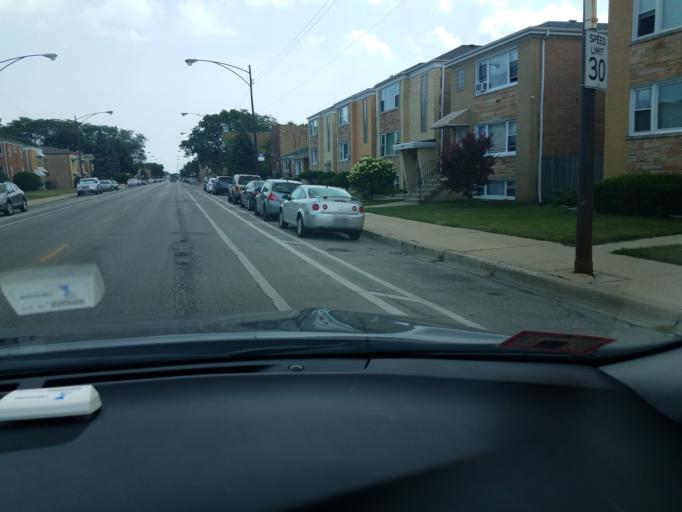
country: US
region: Illinois
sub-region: Cook County
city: Harwood Heights
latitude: 41.9883
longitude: -87.7747
